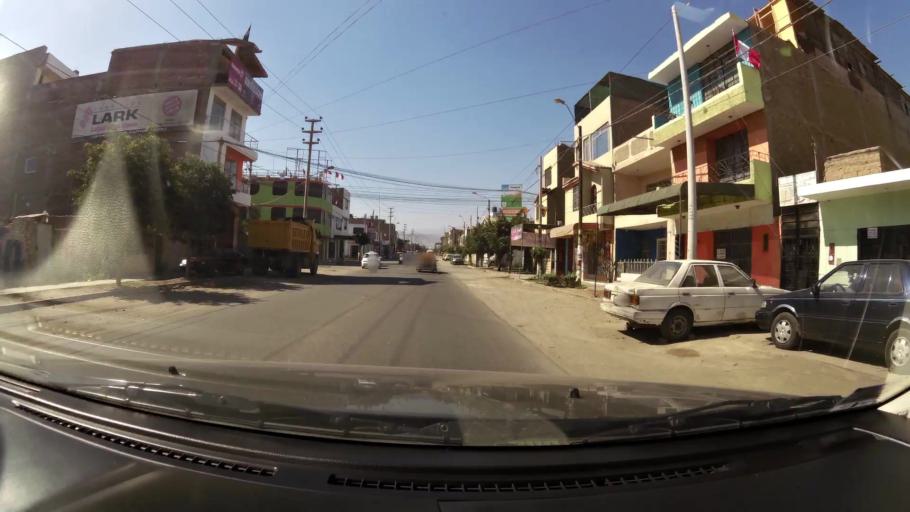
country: PE
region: Ica
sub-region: Provincia de Ica
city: La Tinguina
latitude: -14.0514
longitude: -75.7039
